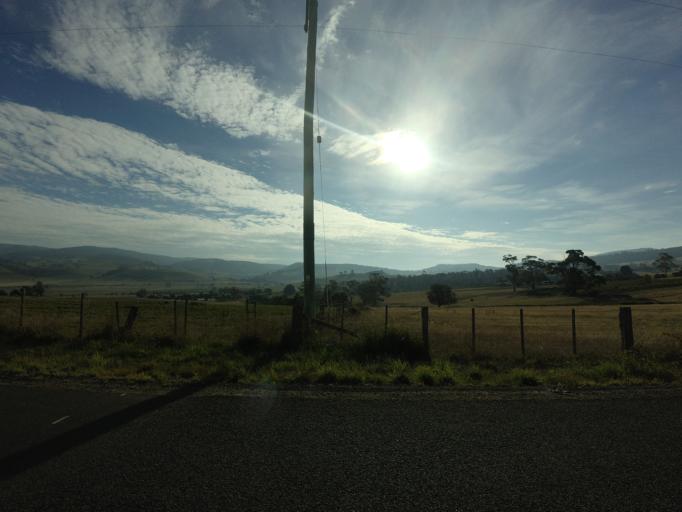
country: AU
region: Tasmania
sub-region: Brighton
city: Bridgewater
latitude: -42.5218
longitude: 147.3771
